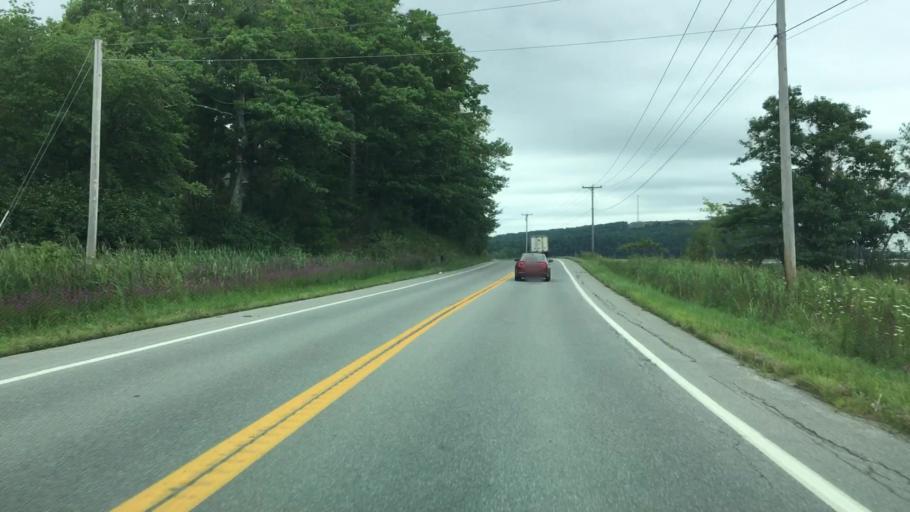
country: US
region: Maine
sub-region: Waldo County
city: Frankfort
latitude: 44.5839
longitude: -68.8634
